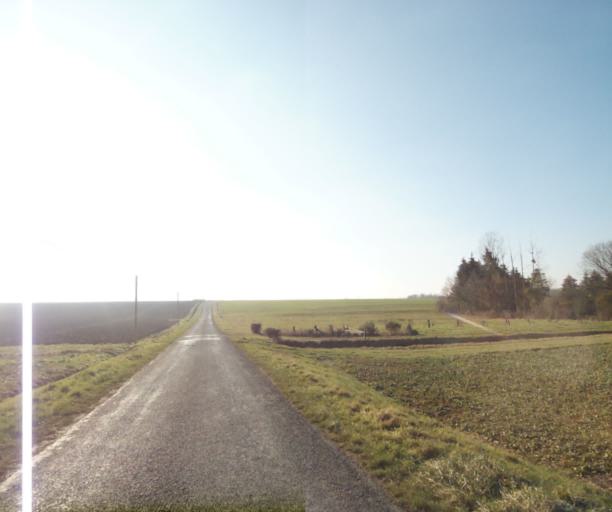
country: FR
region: Champagne-Ardenne
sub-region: Departement de la Haute-Marne
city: Bienville
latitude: 48.5349
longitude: 5.0117
